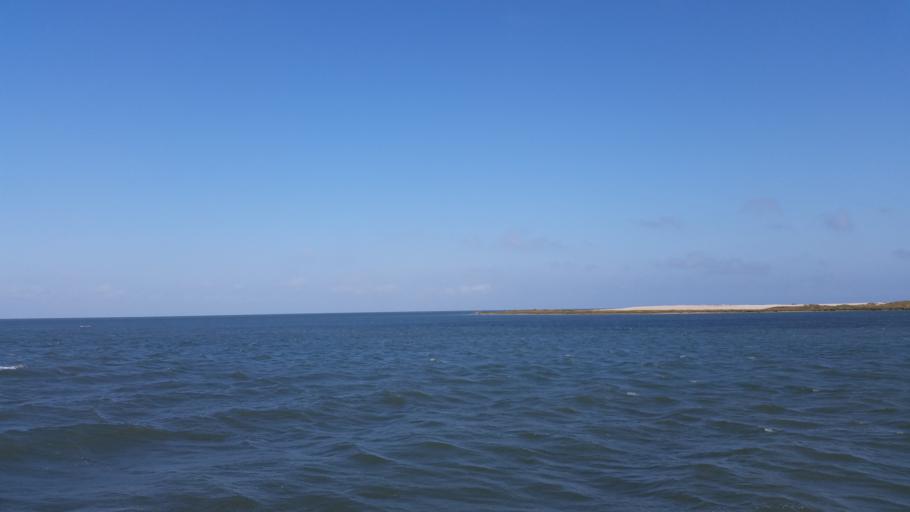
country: US
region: North Carolina
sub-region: Dare County
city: Buxton
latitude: 35.2127
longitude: -75.7151
